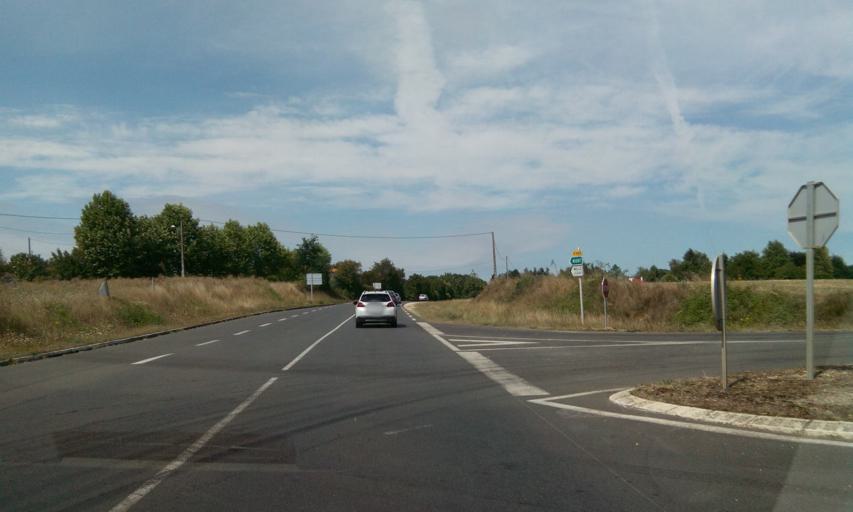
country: FR
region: Poitou-Charentes
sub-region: Departement des Deux-Sevres
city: Sauze-Vaussais
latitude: 46.1385
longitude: 0.1002
